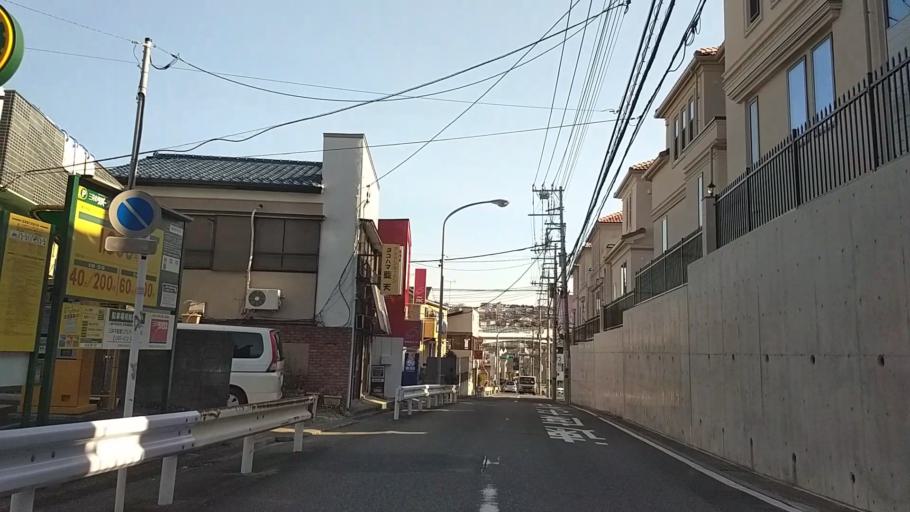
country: JP
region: Kanagawa
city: Yokohama
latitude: 35.3907
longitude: 139.5979
